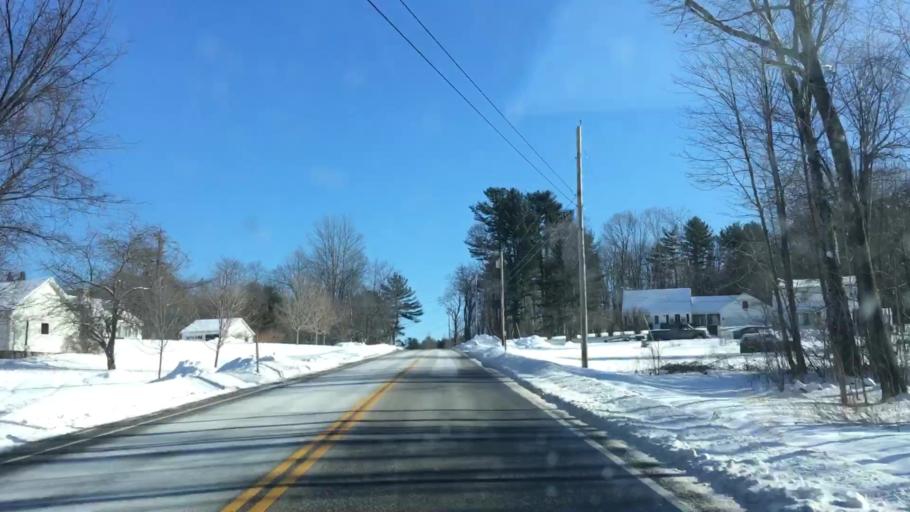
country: US
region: Maine
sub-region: Androscoggin County
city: Lisbon
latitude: 44.0280
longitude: -70.0792
